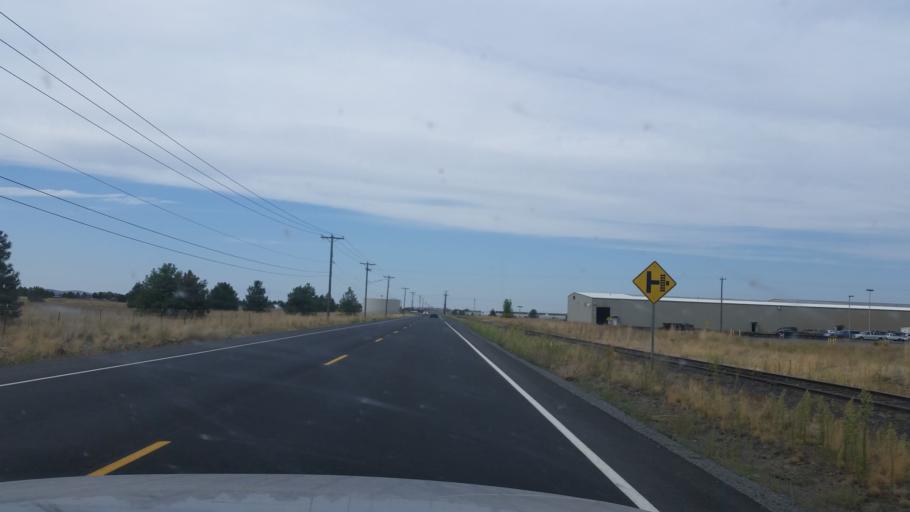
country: US
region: Washington
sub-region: Spokane County
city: Airway Heights
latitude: 47.6284
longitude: -117.5754
